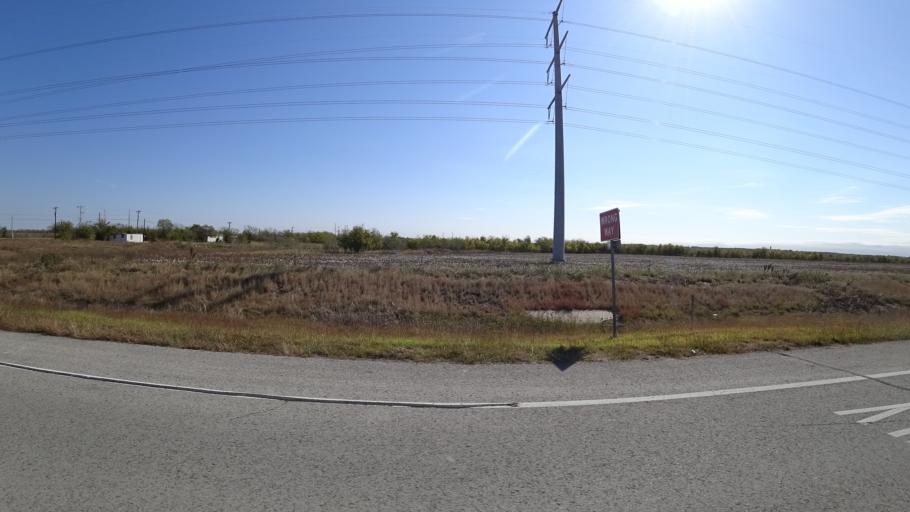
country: US
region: Texas
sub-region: Travis County
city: Onion Creek
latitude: 30.0910
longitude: -97.6791
